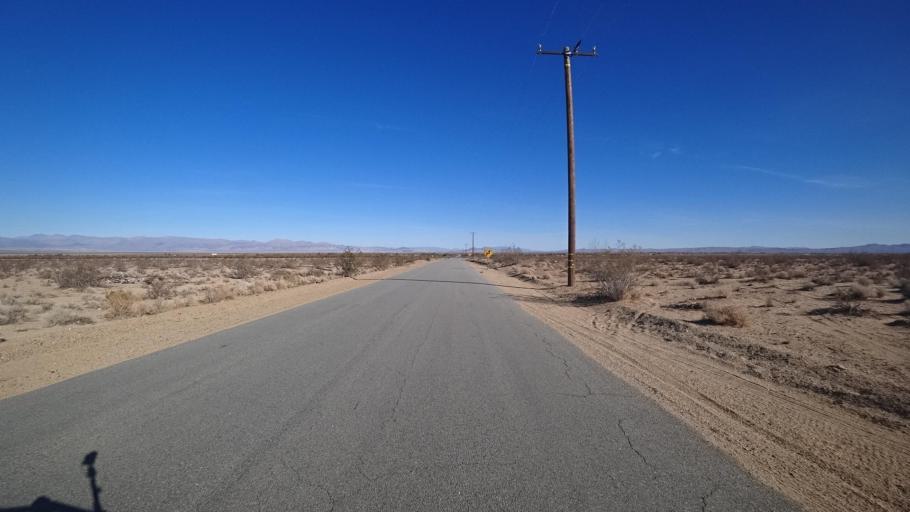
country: US
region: California
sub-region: Kern County
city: Inyokern
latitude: 35.6813
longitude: -117.8462
